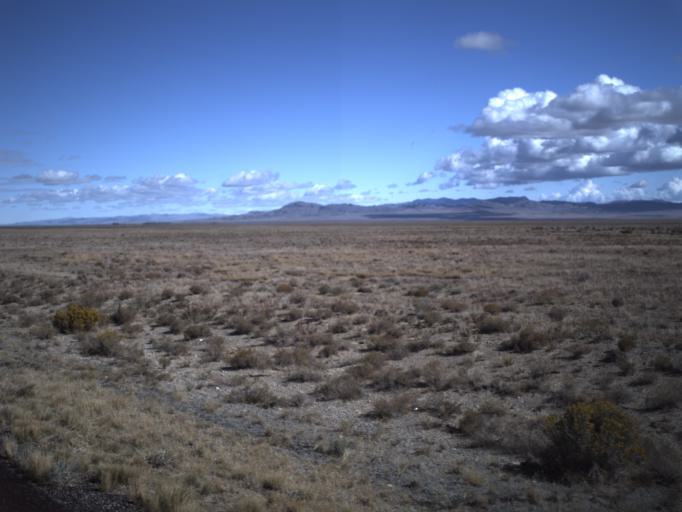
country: US
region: Nevada
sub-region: White Pine County
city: McGill
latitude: 38.9657
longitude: -114.0337
